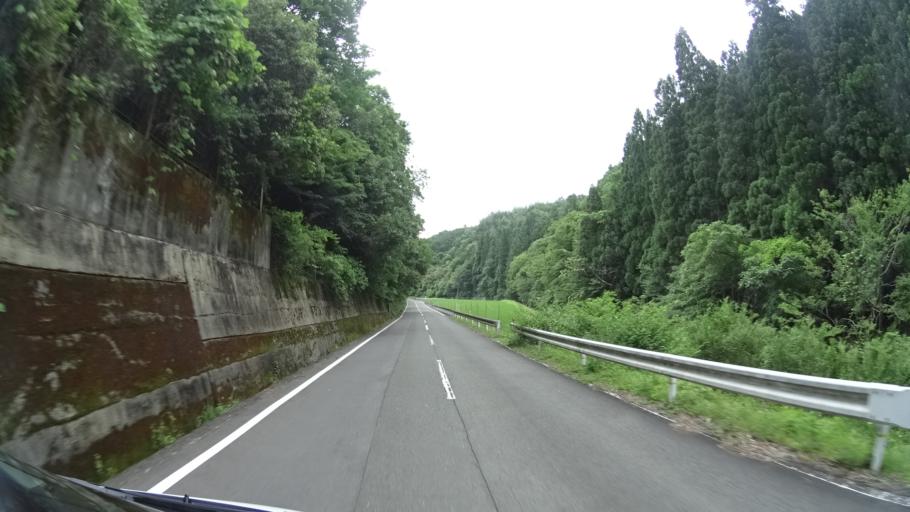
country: JP
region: Hyogo
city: Sasayama
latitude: 35.0632
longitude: 135.3968
